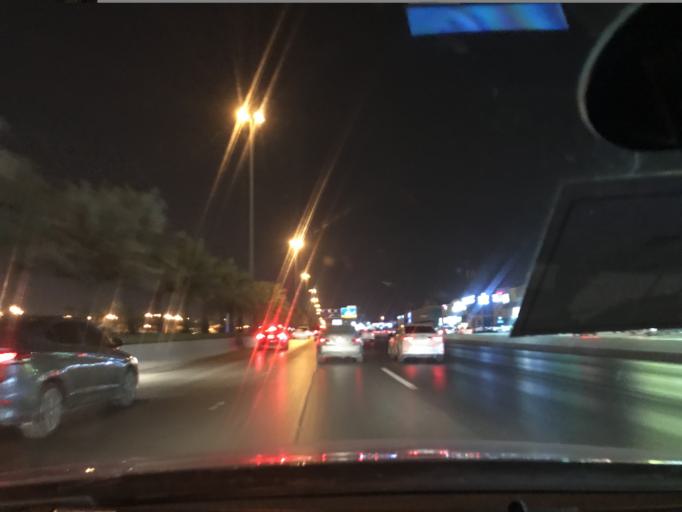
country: SA
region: Ar Riyad
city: Riyadh
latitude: 24.7487
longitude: 46.7446
